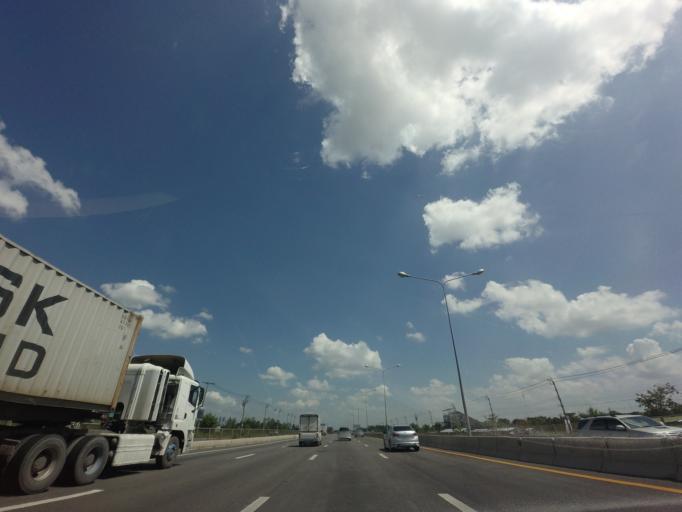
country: TH
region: Bangkok
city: Lat Krabang
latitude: 13.7324
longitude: 100.7849
